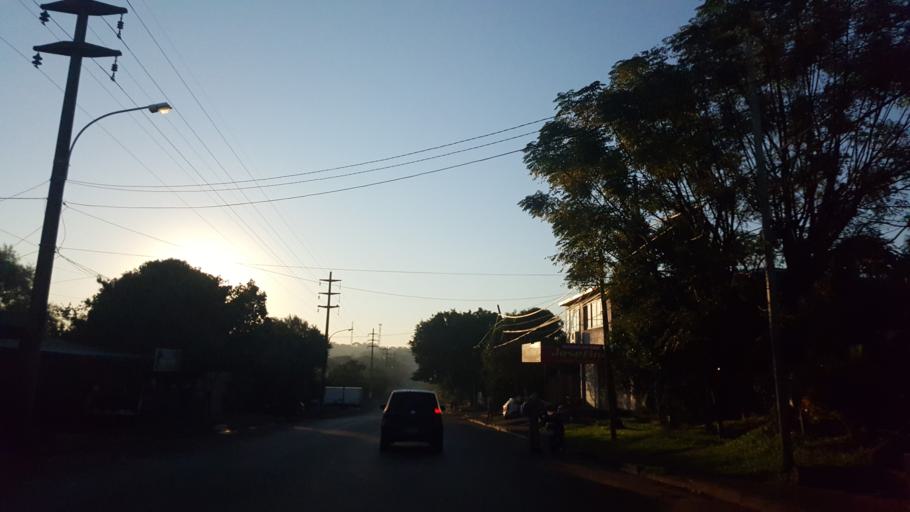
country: AR
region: Misiones
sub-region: Departamento de Capital
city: Posadas
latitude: -27.3732
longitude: -55.9390
